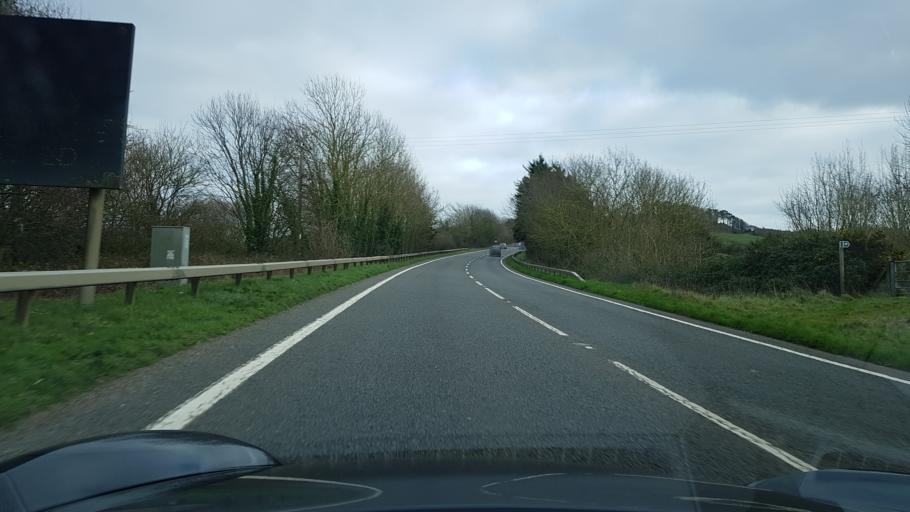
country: GB
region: England
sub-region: Dorset
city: Bridport
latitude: 50.7330
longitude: -2.6958
